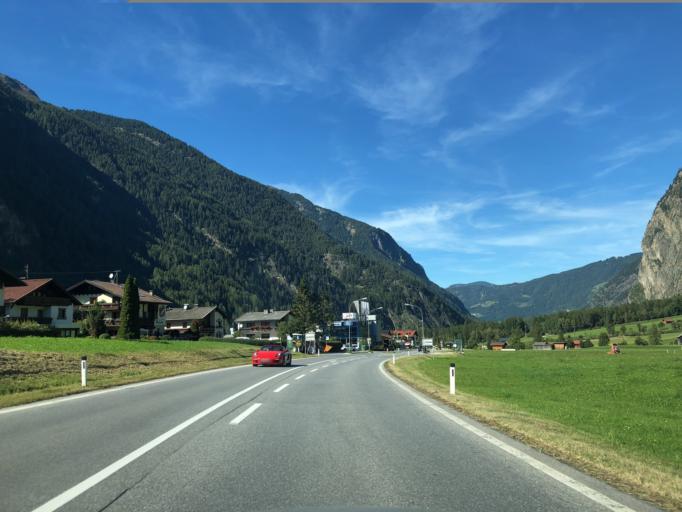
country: AT
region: Tyrol
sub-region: Politischer Bezirk Imst
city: Umhausen
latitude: 47.1436
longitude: 10.9178
